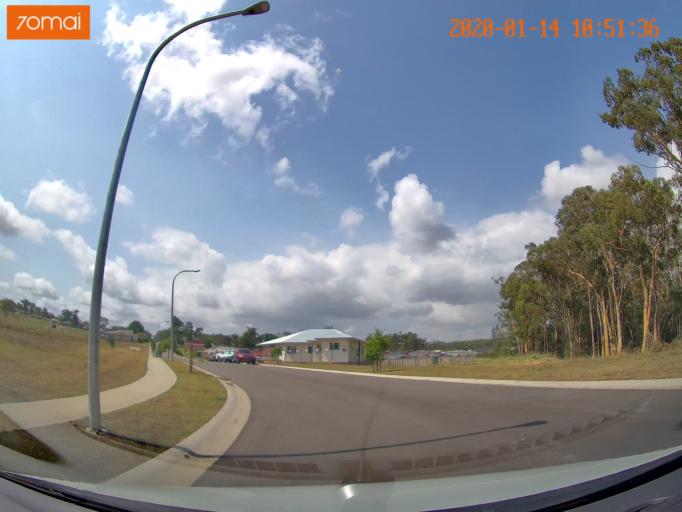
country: AU
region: New South Wales
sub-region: Lake Macquarie Shire
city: Dora Creek
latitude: -33.0981
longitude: 151.4838
